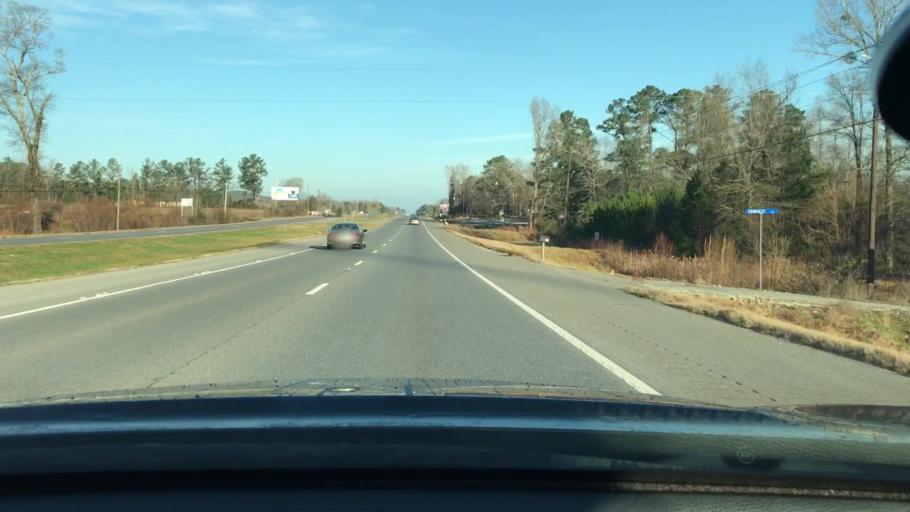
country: US
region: Alabama
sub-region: Talladega County
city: Childersburg
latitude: 33.2254
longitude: -86.3225
